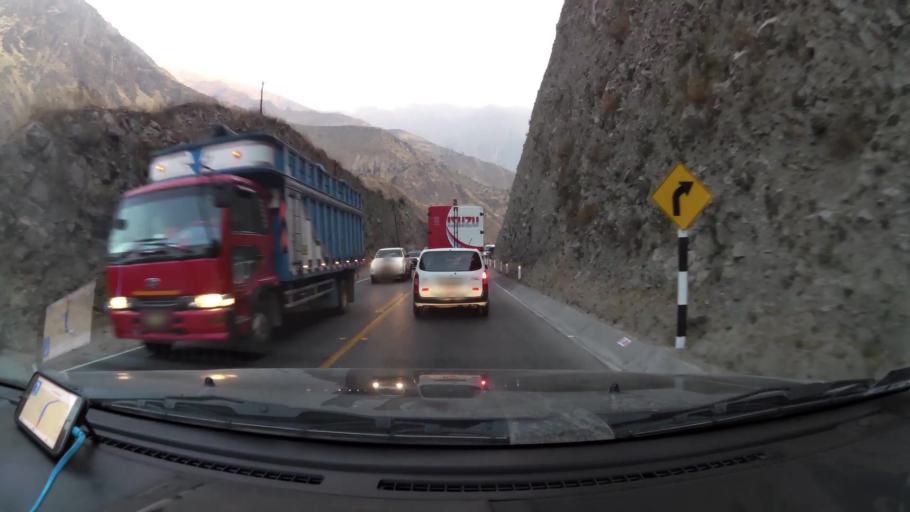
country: PE
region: Lima
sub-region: Provincia de Huarochiri
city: Surco
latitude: -11.8694
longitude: -76.4259
